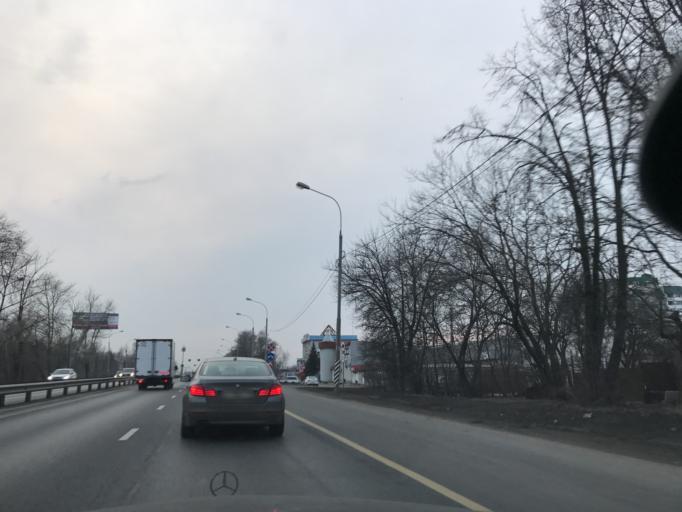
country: RU
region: Moskovskaya
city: Obukhovo
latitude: 55.8289
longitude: 38.2693
